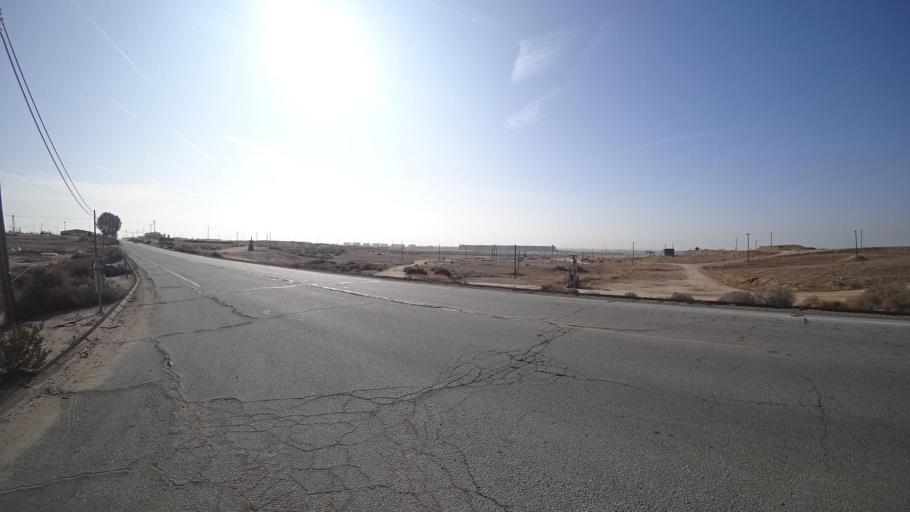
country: US
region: California
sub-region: Kern County
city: Oildale
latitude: 35.4600
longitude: -119.0492
